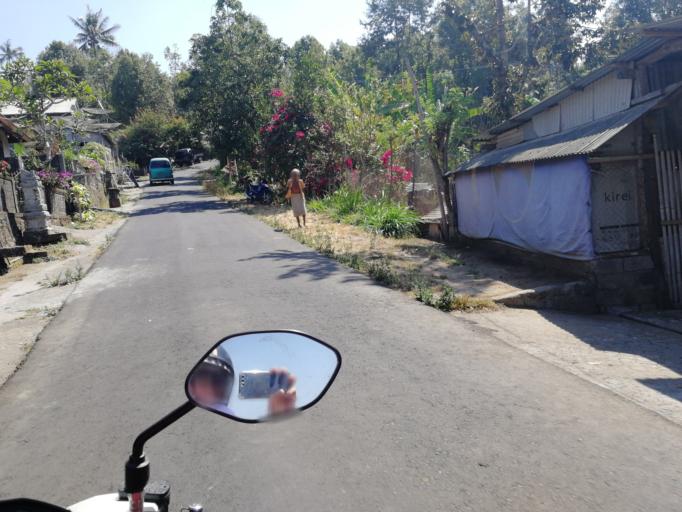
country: ID
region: Bali
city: Banjar Kedisan
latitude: -8.1584
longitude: 115.3060
